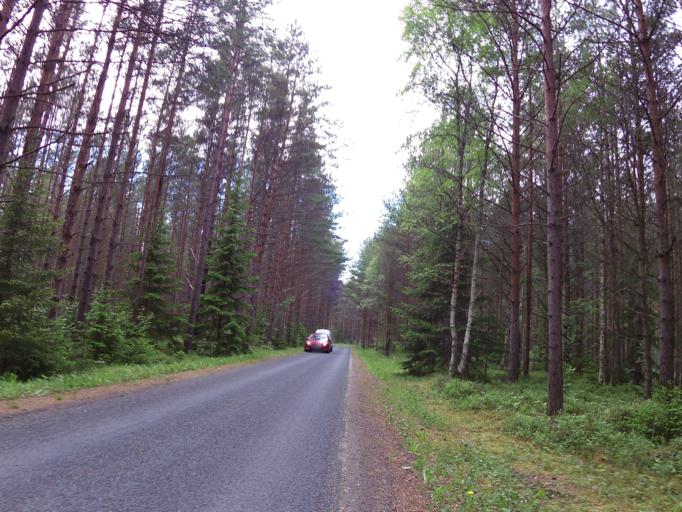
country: EE
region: Harju
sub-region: Paldiski linn
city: Paldiski
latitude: 59.2513
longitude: 23.7638
